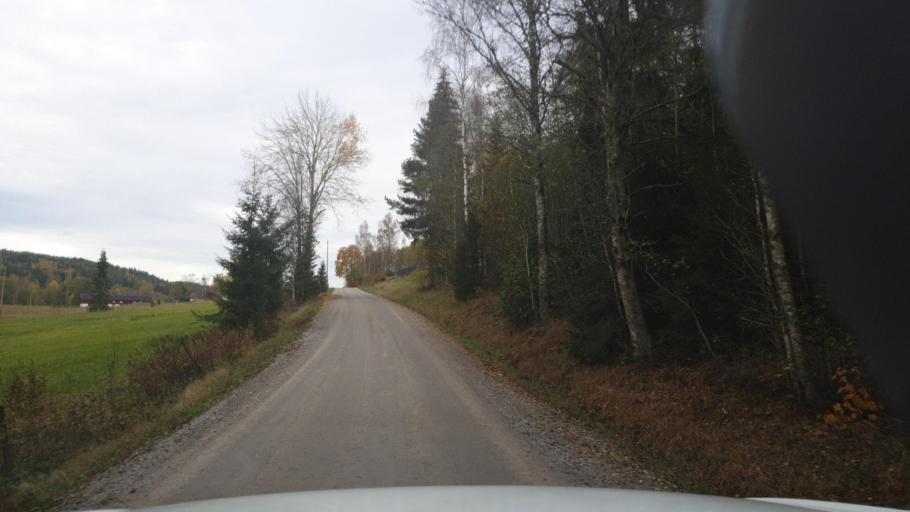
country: SE
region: Vaermland
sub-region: Arvika Kommun
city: Arvika
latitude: 59.6849
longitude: 12.7727
